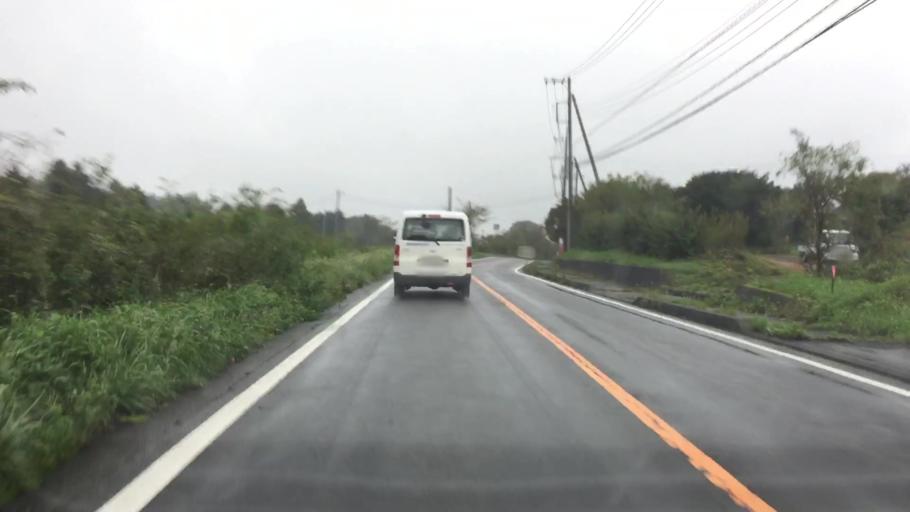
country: JP
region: Yamanashi
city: Fujikawaguchiko
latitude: 35.4185
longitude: 138.6242
